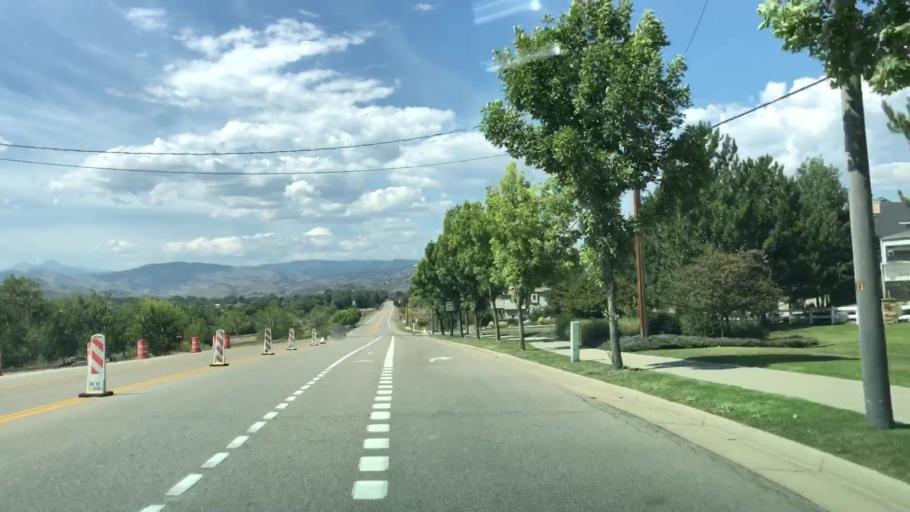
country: US
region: Colorado
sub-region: Larimer County
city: Loveland
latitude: 40.3930
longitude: -105.1394
